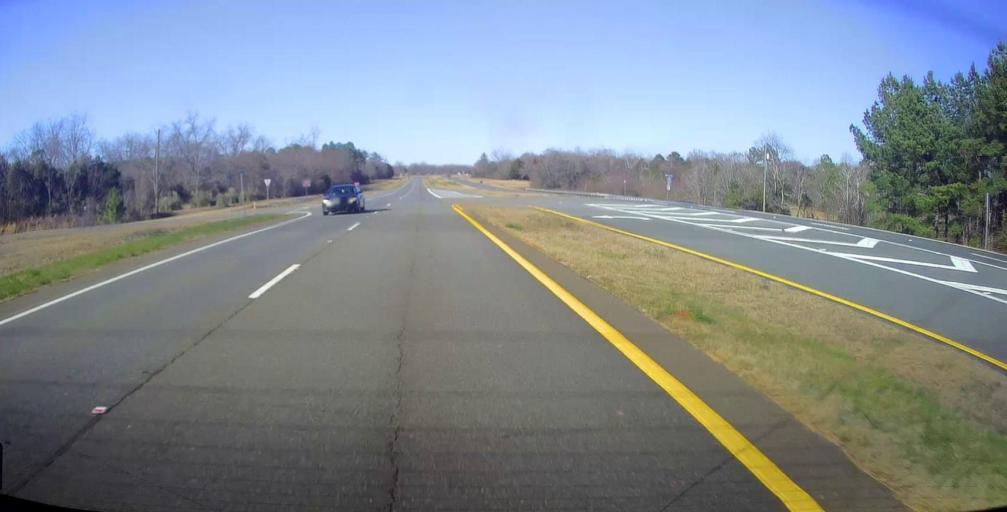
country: US
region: Georgia
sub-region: Sumter County
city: Americus
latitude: 32.1491
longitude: -84.2695
